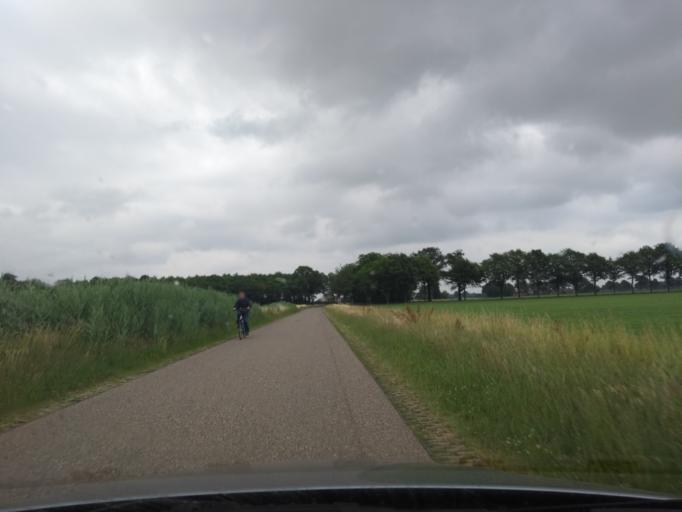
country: NL
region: Overijssel
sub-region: Gemeente Hof van Twente
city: Markelo
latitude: 52.2045
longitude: 6.4594
